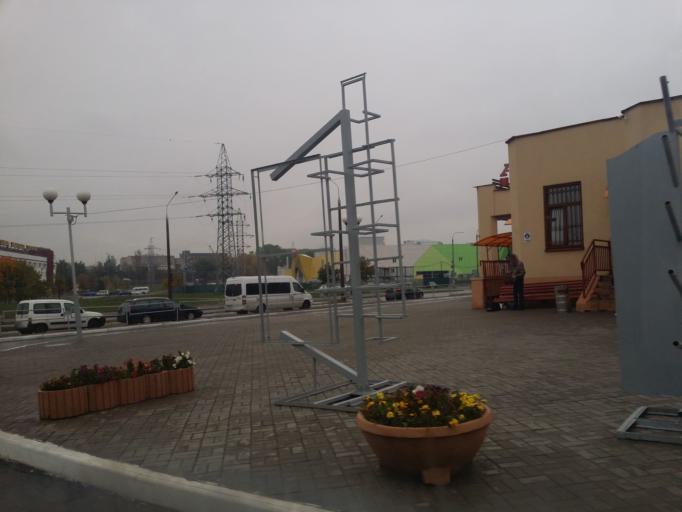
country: BY
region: Minsk
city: Vyaliki Trastsyanets
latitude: 53.8581
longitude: 27.6772
